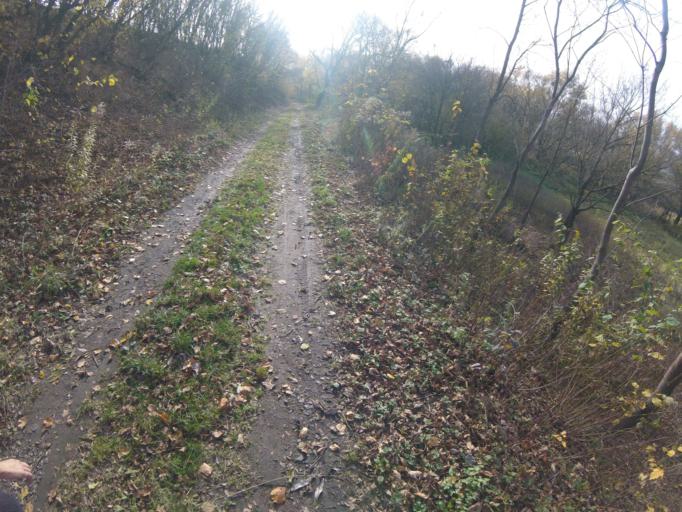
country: HU
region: Borsod-Abauj-Zemplen
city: Gonc
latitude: 48.5079
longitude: 21.4537
